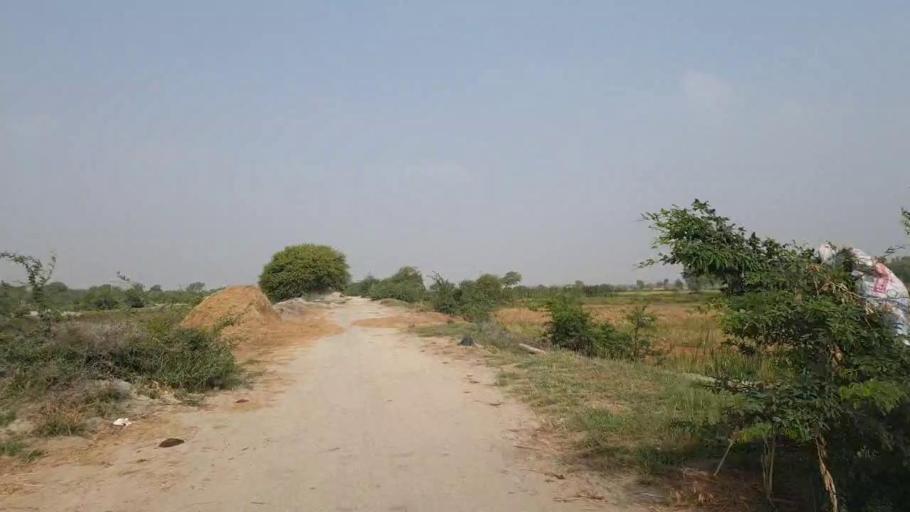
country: PK
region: Sindh
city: Kario
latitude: 24.7745
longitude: 68.5224
